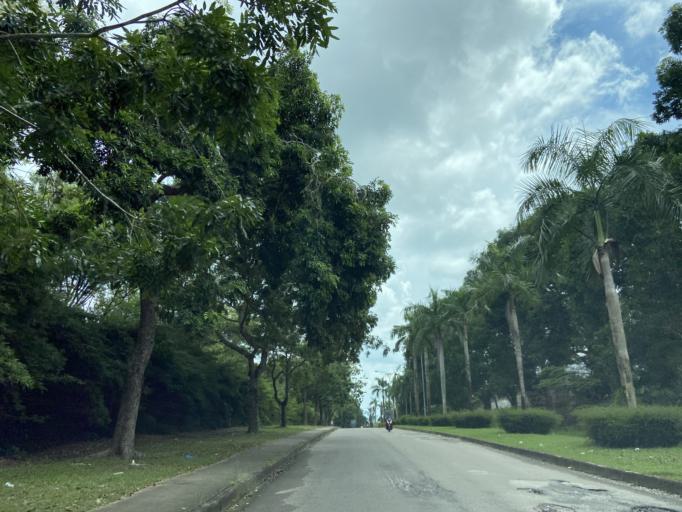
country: SG
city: Singapore
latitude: 1.1301
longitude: 104.0012
